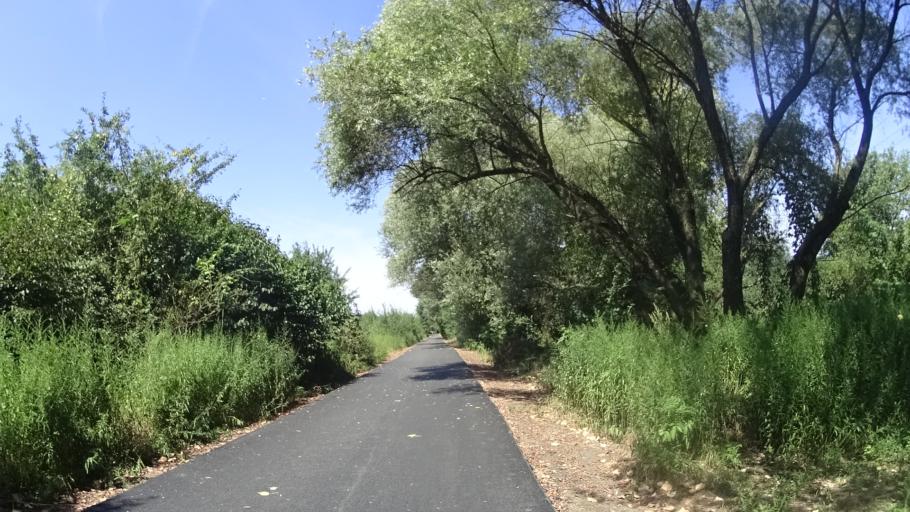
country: AT
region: Lower Austria
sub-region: Politischer Bezirk Bruck an der Leitha
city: Hainburg an der Donau
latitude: 48.2085
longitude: 16.9691
